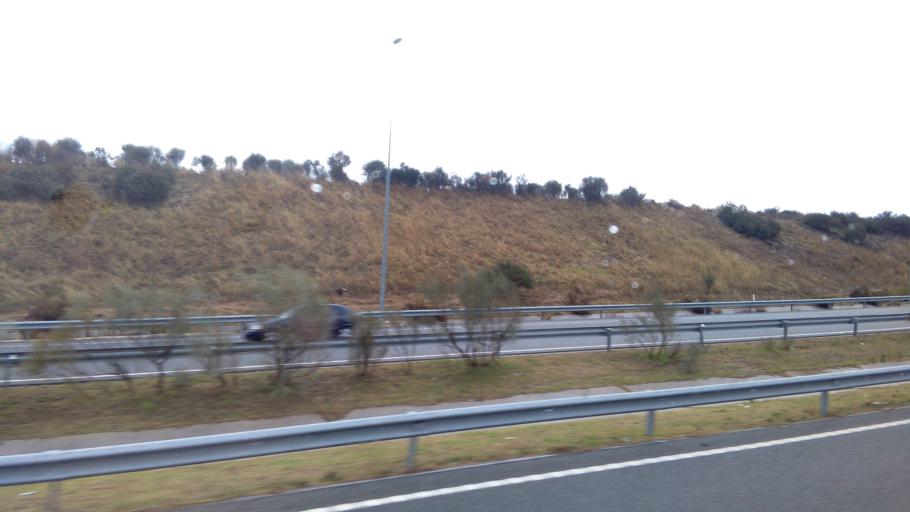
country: ES
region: Madrid
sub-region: Provincia de Madrid
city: Alcorcon
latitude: 40.3342
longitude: -3.8107
